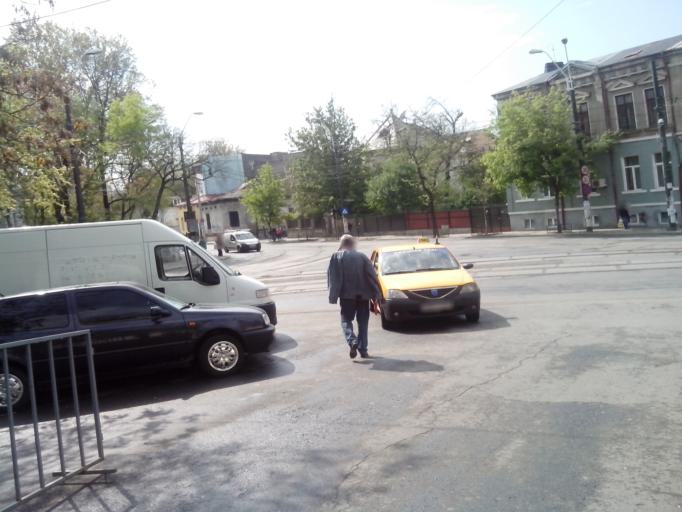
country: RO
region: Bucuresti
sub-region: Municipiul Bucuresti
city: Bucuresti
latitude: 44.4240
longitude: 26.0957
